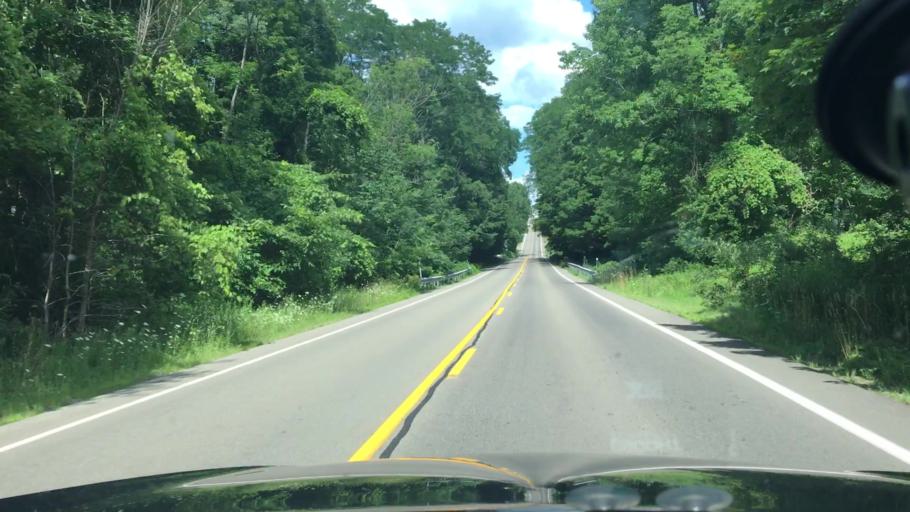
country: US
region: New York
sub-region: Chautauqua County
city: Lakewood
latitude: 42.1774
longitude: -79.3621
